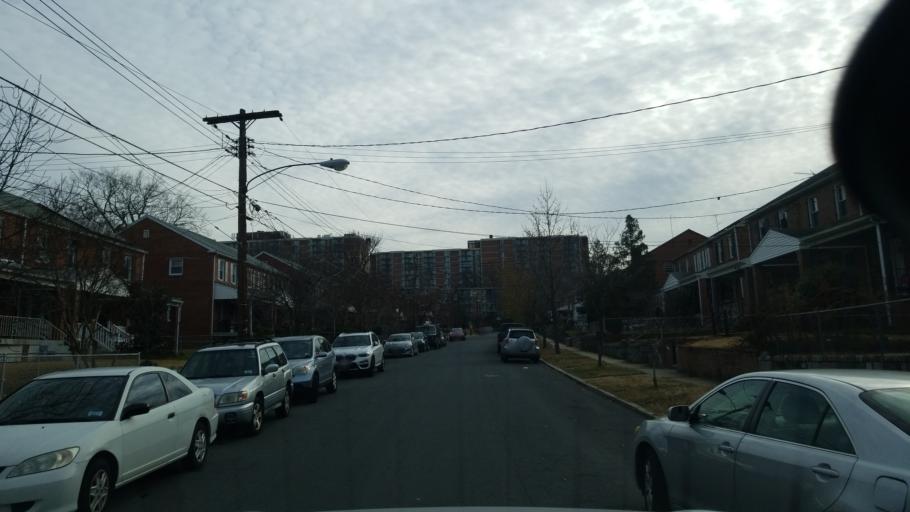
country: US
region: Maryland
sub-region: Prince George's County
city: Hillcrest Heights
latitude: 38.8662
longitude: -76.9775
